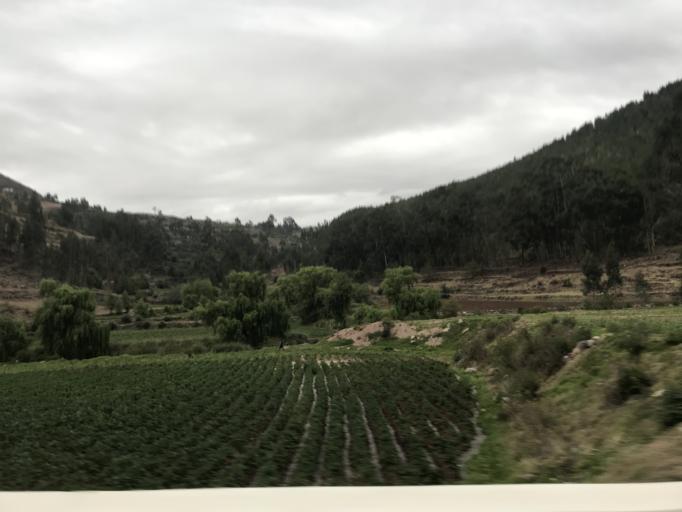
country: PE
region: Cusco
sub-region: Provincia de Anta
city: Huarocondo
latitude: -13.4004
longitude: -72.2101
